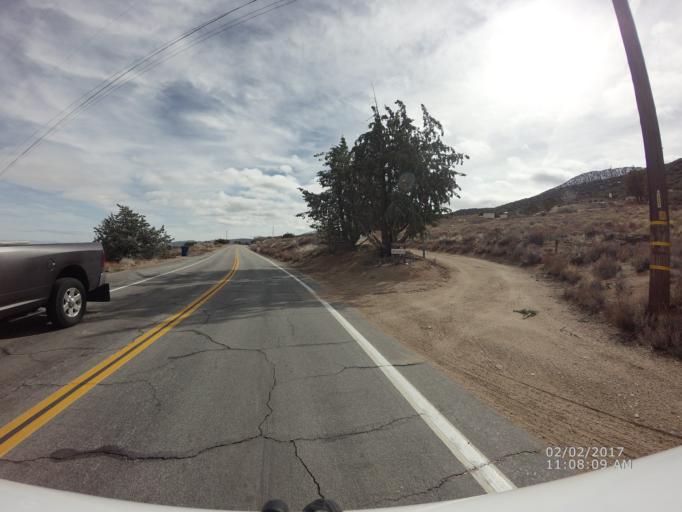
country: US
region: California
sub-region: Los Angeles County
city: Littlerock
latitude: 34.4341
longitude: -117.9293
